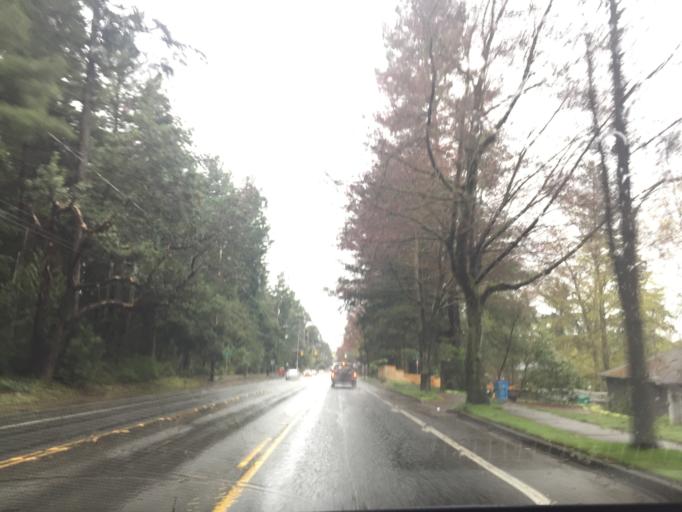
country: US
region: Washington
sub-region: King County
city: Shoreline
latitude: 47.7467
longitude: -122.3132
